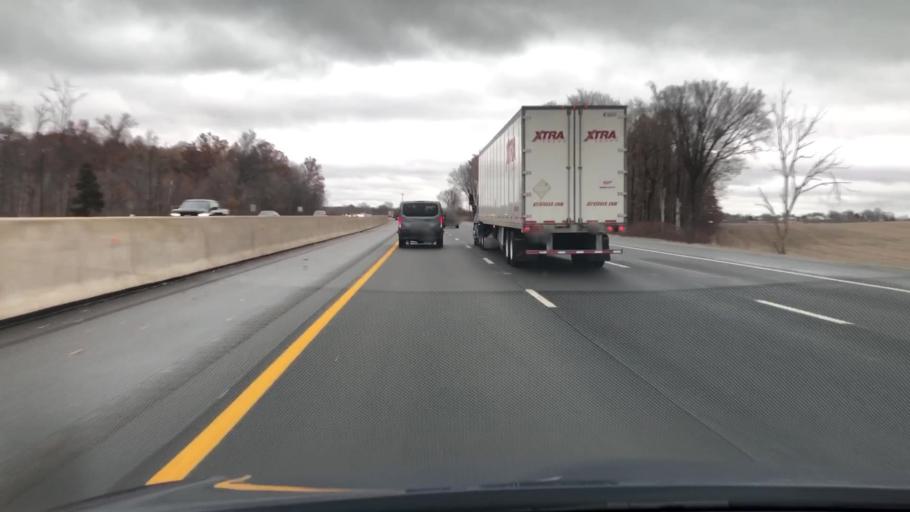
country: US
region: Ohio
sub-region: Lorain County
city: South Amherst
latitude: 41.3460
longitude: -82.3245
